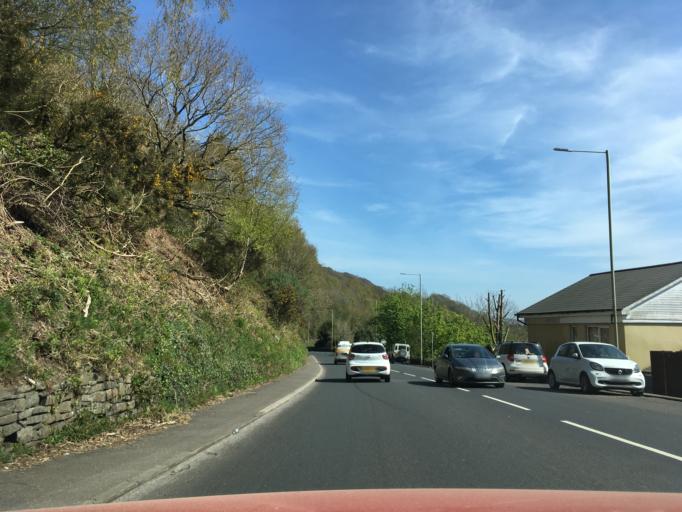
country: GB
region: Wales
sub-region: Rhondda Cynon Taf
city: Pontypridd
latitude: 51.6035
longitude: -3.3333
